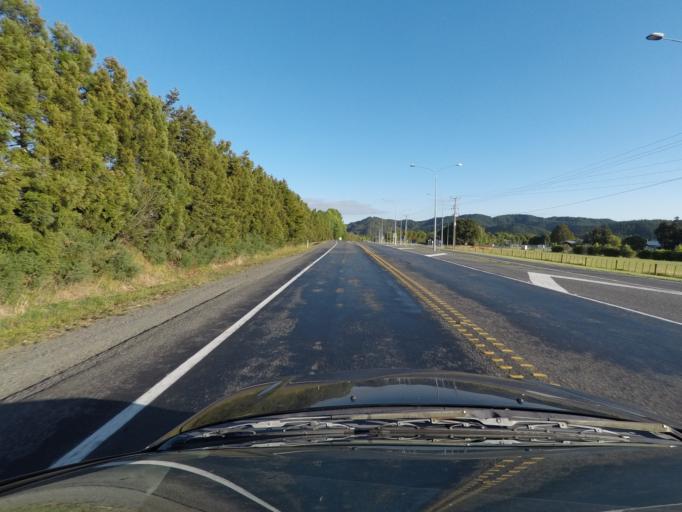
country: NZ
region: Northland
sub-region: Whangarei
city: Whangarei
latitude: -35.6364
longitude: 174.2964
